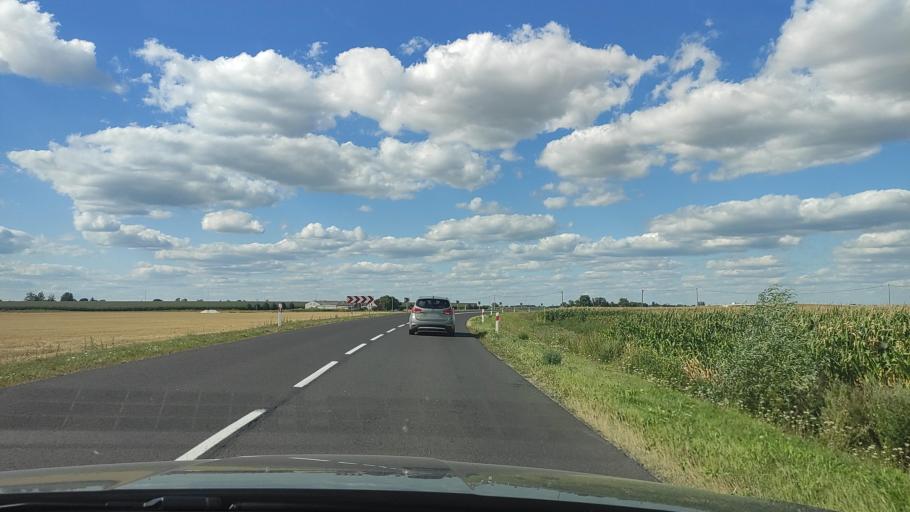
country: PL
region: Greater Poland Voivodeship
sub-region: Powiat poznanski
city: Kleszczewo
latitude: 52.3323
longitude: 17.1596
